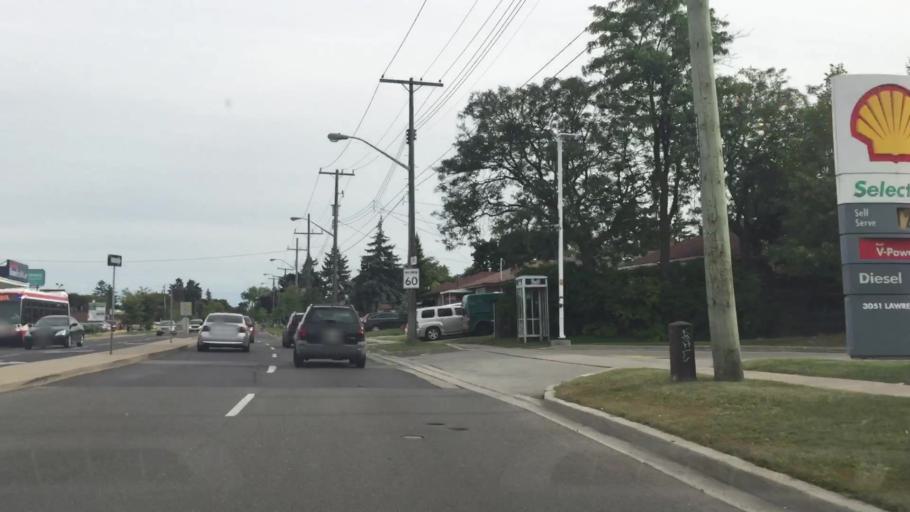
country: CA
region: Ontario
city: Scarborough
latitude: 43.7552
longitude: -79.2455
